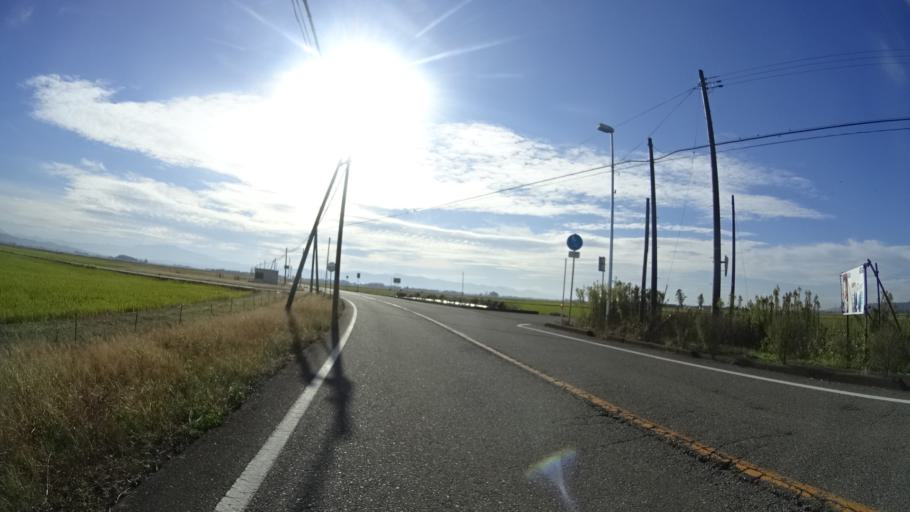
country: JP
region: Niigata
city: Mitsuke
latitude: 37.5701
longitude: 138.8420
